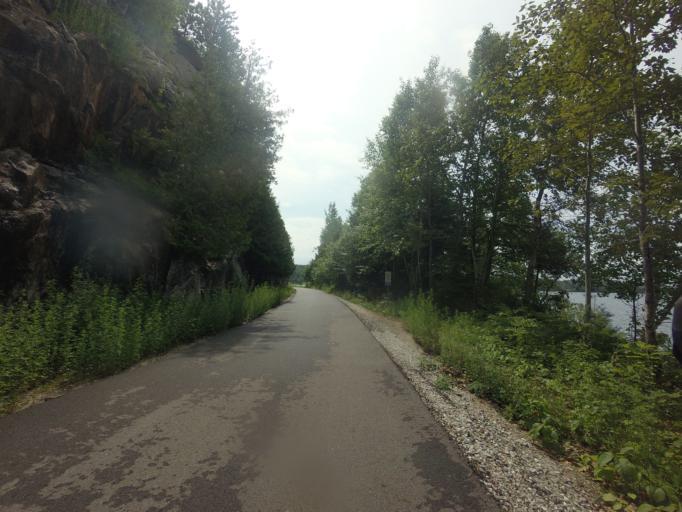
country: CA
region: Quebec
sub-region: Outaouais
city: Maniwaki
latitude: 46.2144
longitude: -76.0437
